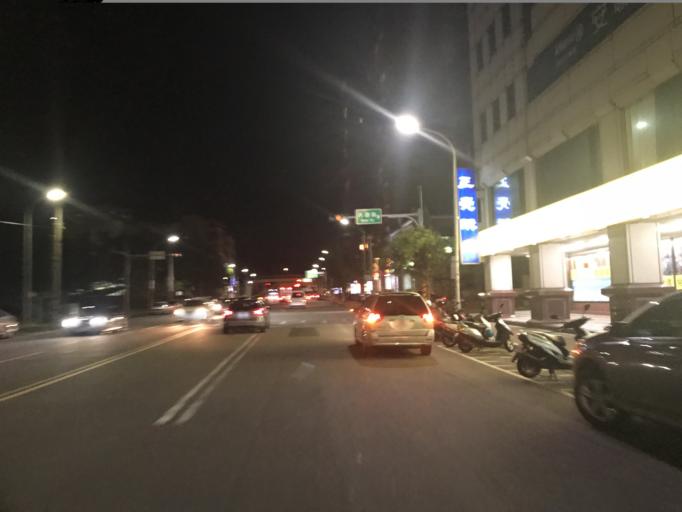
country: TW
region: Taiwan
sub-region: Hsinchu
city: Hsinchu
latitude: 24.8033
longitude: 120.9868
